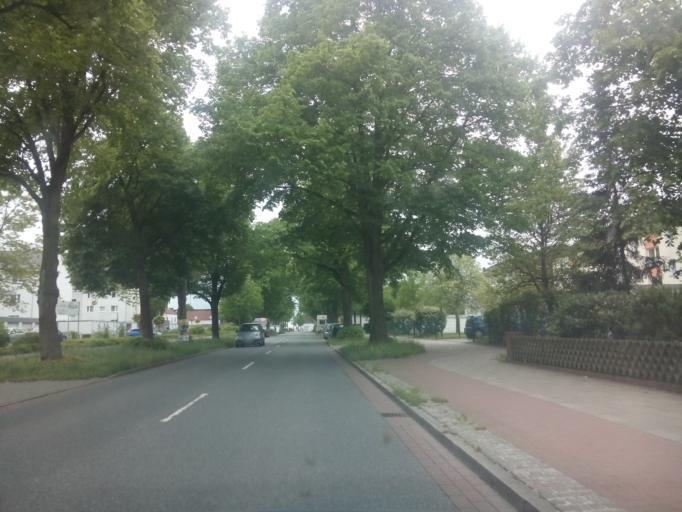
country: DE
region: Lower Saxony
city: Schwanewede
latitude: 53.2096
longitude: 8.5788
